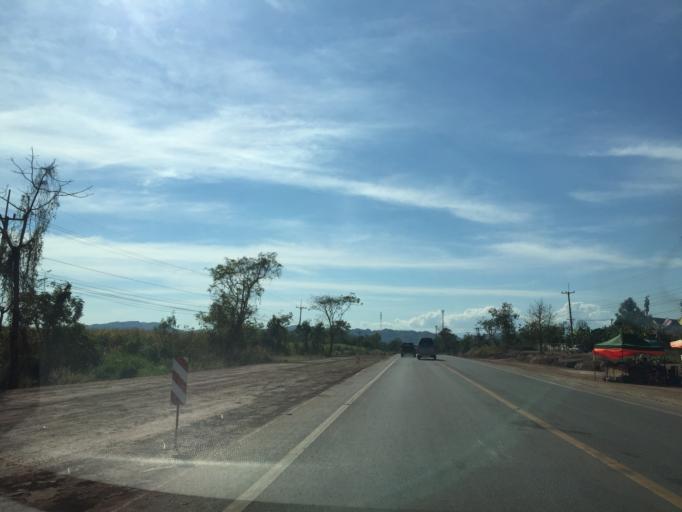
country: TH
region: Loei
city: Erawan
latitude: 17.3033
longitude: 101.8859
